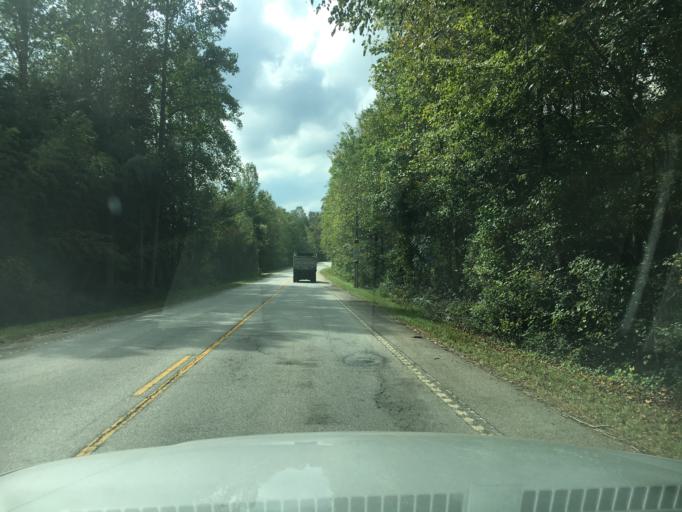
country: US
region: South Carolina
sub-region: Greenville County
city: Tigerville
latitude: 35.0486
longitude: -82.2609
